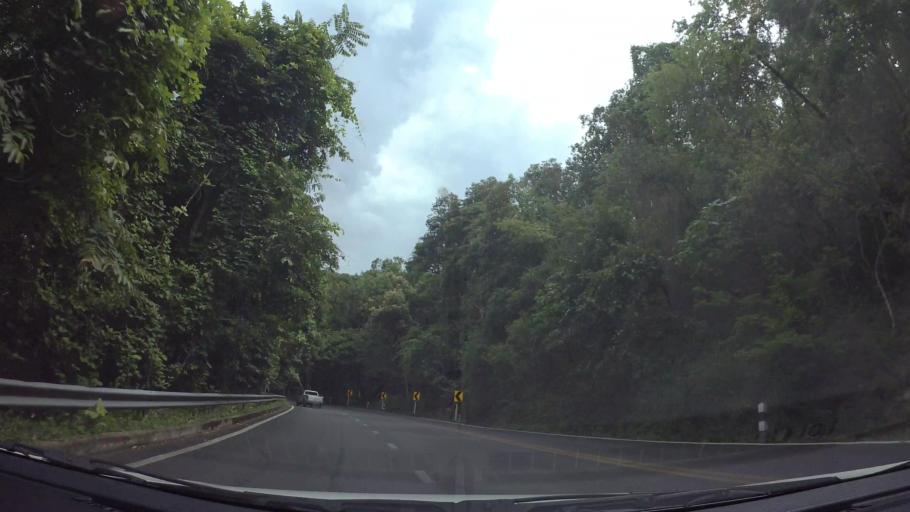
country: TH
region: Chiang Mai
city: Chiang Mai
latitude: 18.8047
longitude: 98.9343
